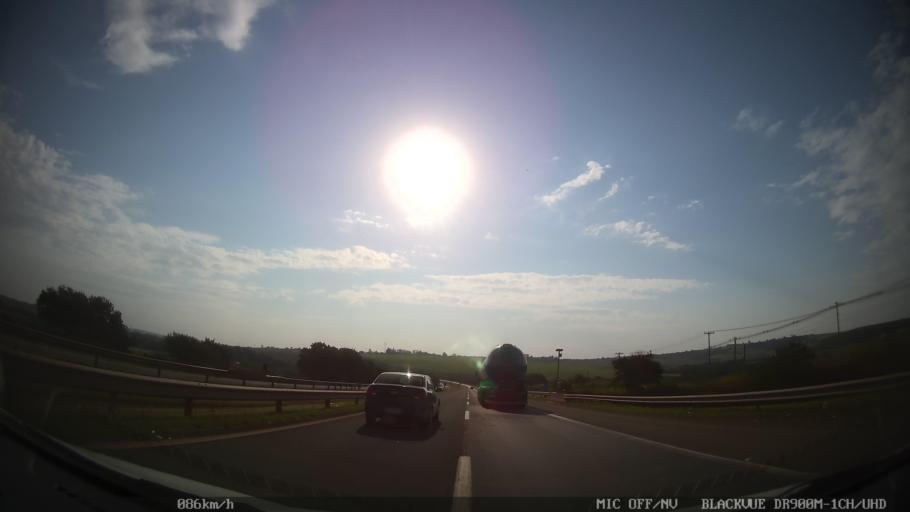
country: BR
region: Sao Paulo
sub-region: Cosmopolis
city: Cosmopolis
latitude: -22.6608
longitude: -47.1694
